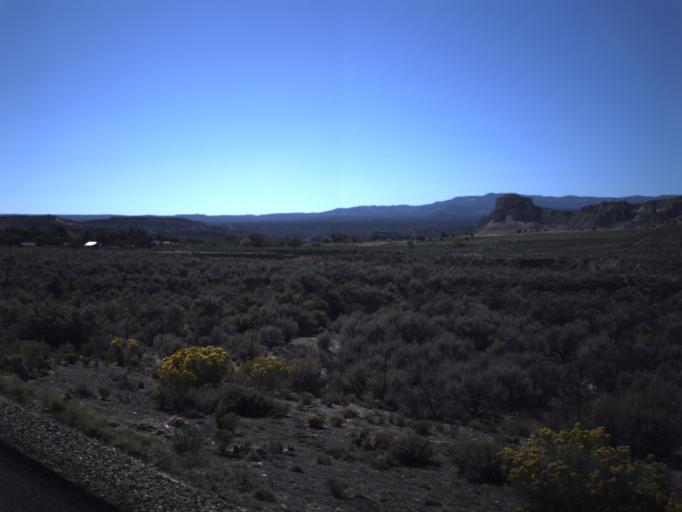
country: US
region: Utah
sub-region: Garfield County
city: Panguitch
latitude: 37.5725
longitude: -111.9883
